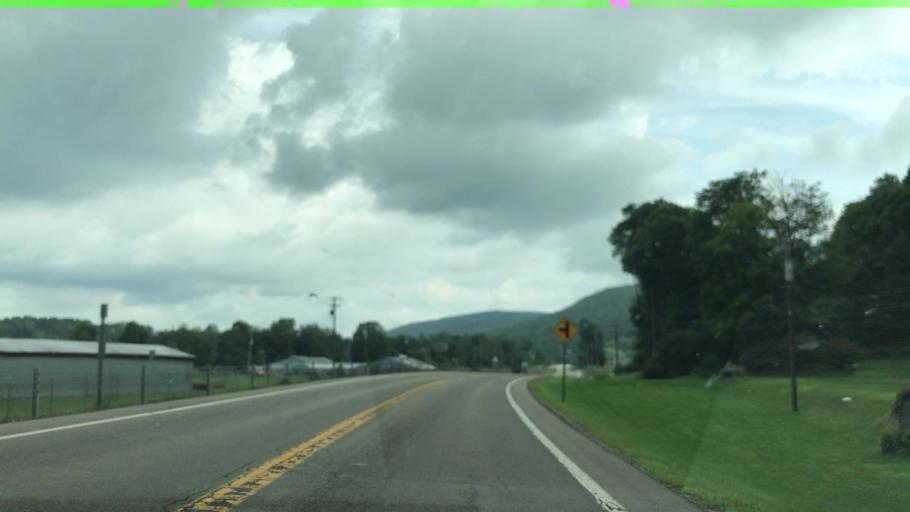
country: US
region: New York
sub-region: Steuben County
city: Bath
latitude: 42.3853
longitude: -77.3575
